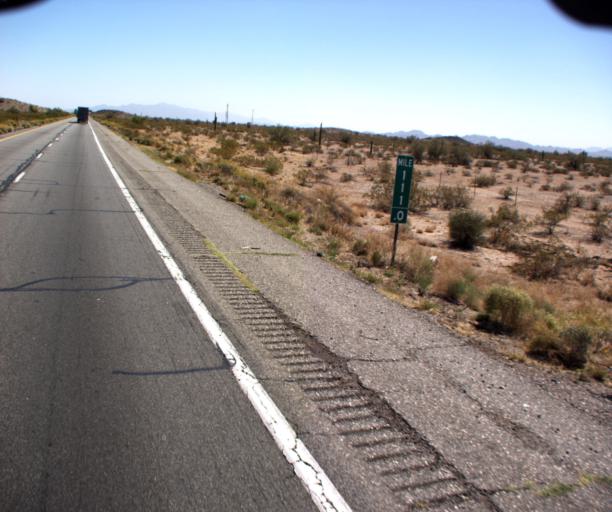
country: US
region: Arizona
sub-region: Maricopa County
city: Buckeye
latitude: 33.4341
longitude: -112.6556
